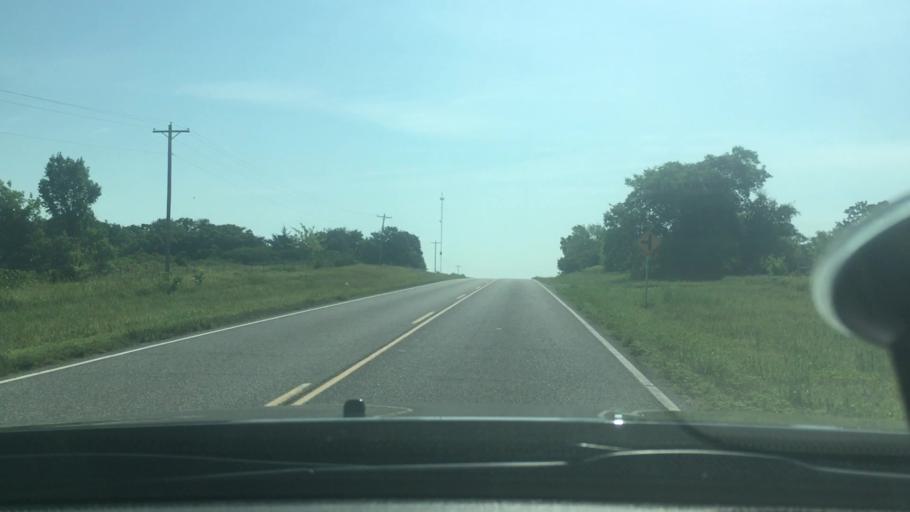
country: US
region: Oklahoma
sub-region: Garvin County
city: Pauls Valley
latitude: 34.6517
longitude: -97.2697
